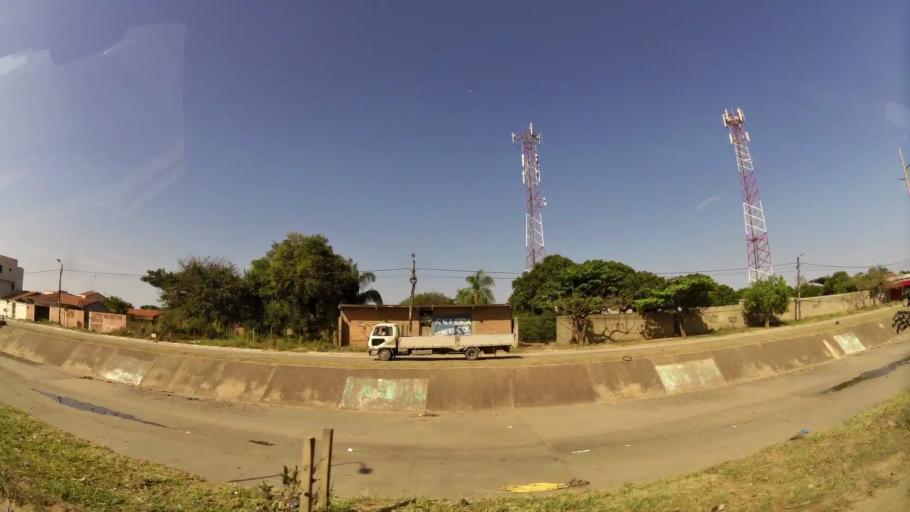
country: BO
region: Santa Cruz
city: Cotoca
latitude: -17.7947
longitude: -63.1057
